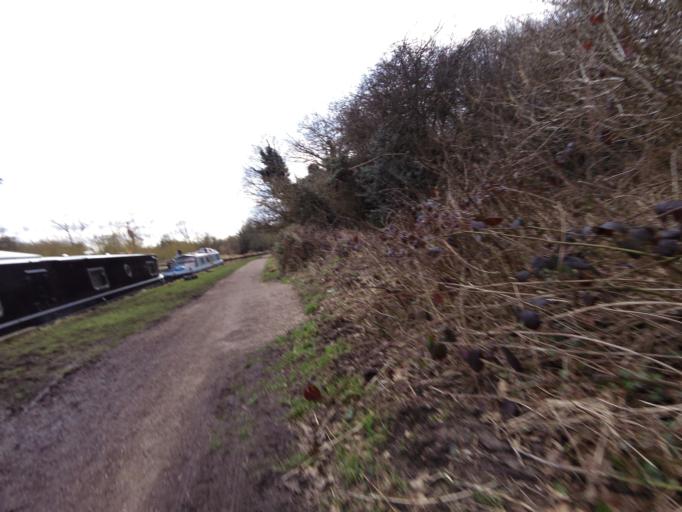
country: GB
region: England
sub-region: Hertfordshire
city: Watford
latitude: 51.6635
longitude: -0.4270
